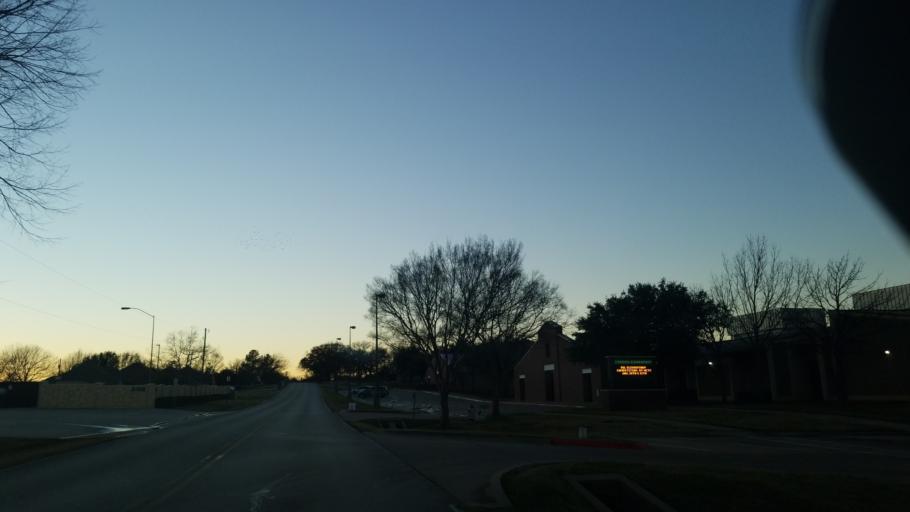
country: US
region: Texas
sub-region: Denton County
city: Hickory Creek
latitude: 33.1324
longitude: -97.0518
